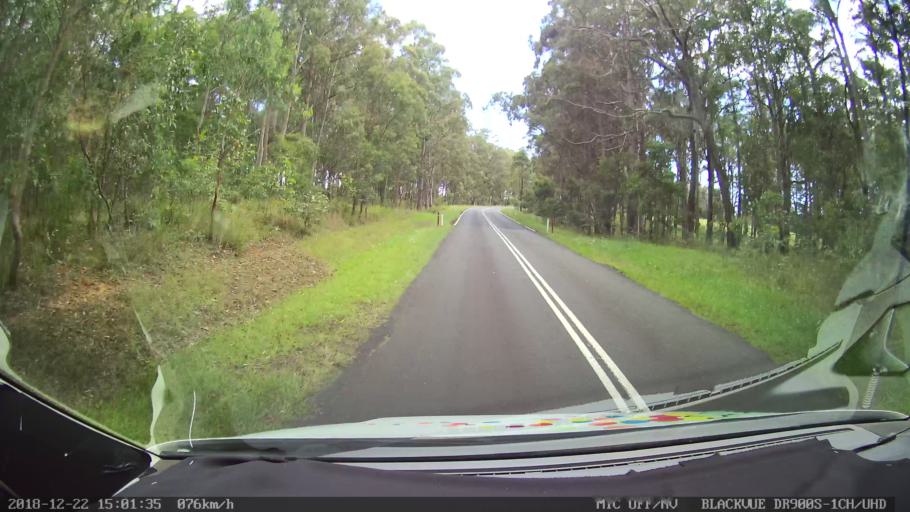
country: AU
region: New South Wales
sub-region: Bellingen
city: Dorrigo
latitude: -30.2561
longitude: 152.4580
